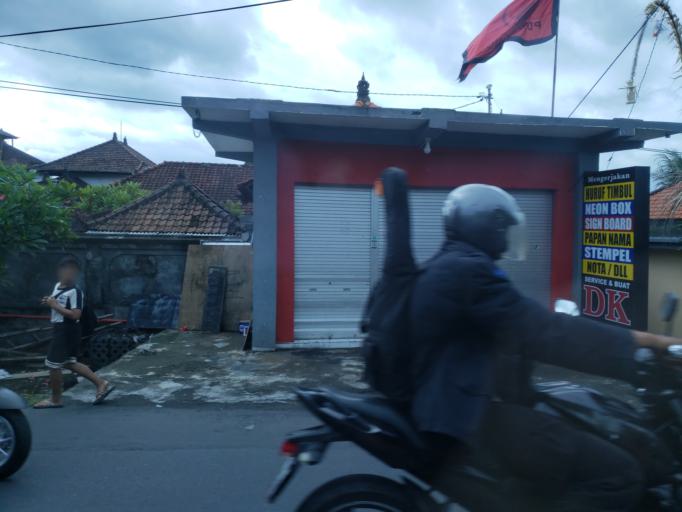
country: ID
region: Bali
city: Dajan Tangluk
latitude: -8.6469
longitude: 115.2427
